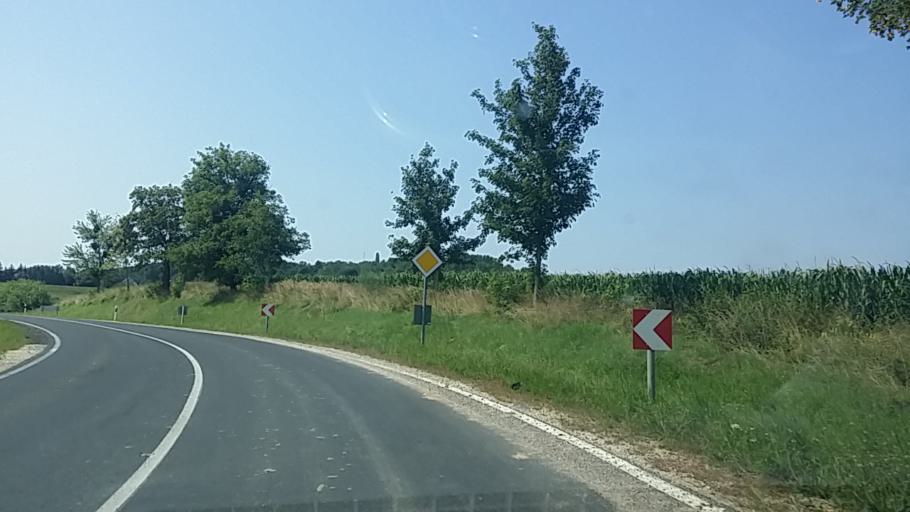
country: HU
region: Zala
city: Lenti
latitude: 46.5700
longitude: 16.5547
